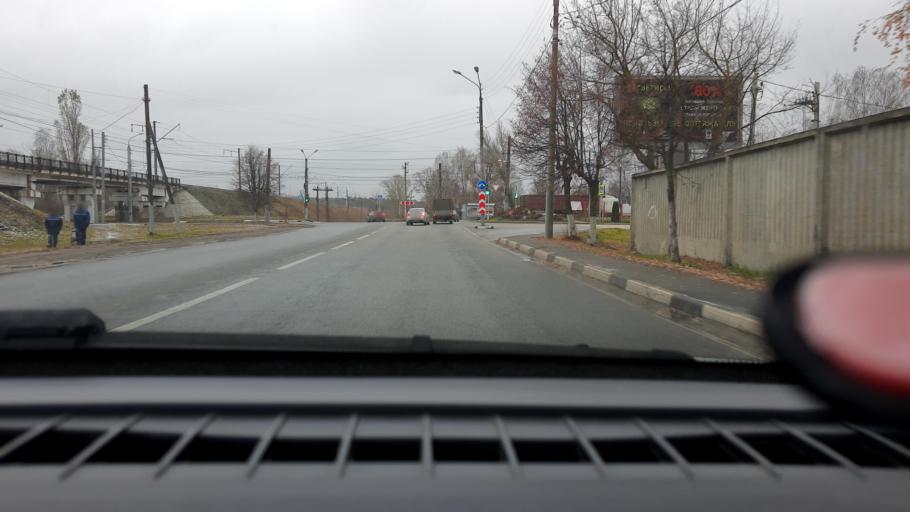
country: RU
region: Nizjnij Novgorod
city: Burevestnik
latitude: 56.2077
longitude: 43.8043
